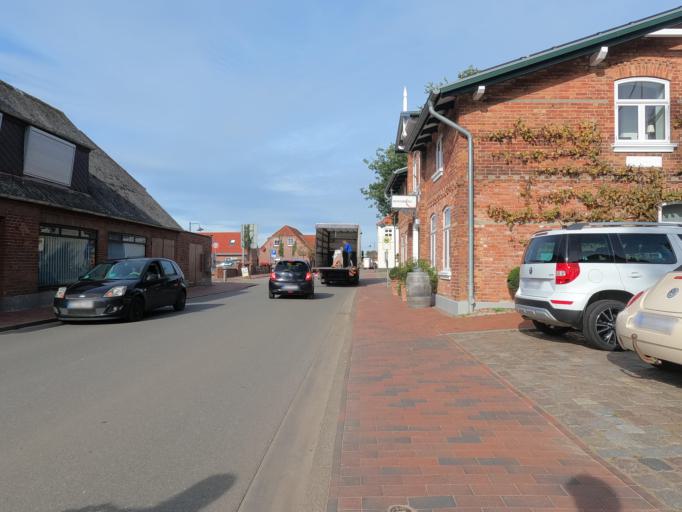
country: DE
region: Schleswig-Holstein
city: Grube
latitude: 54.2304
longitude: 11.0361
